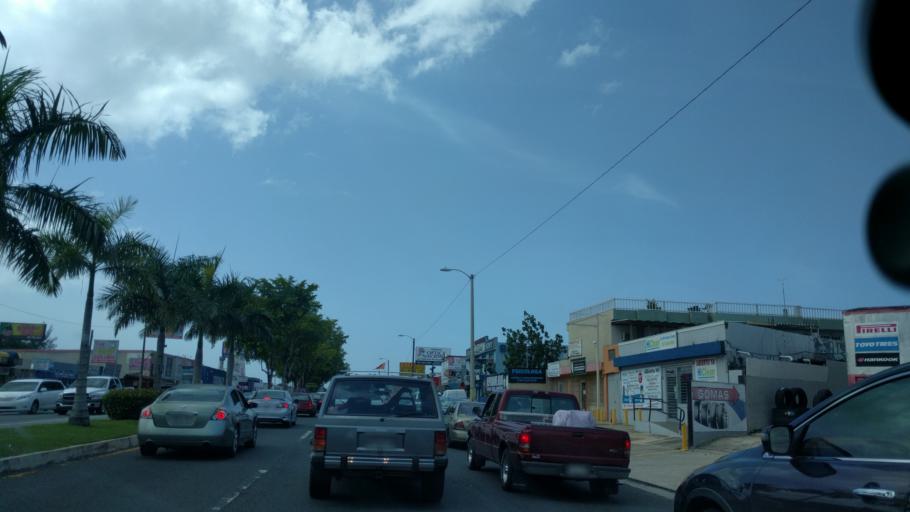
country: PR
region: Bayamon
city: Bayamon
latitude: 18.4157
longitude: -66.1620
